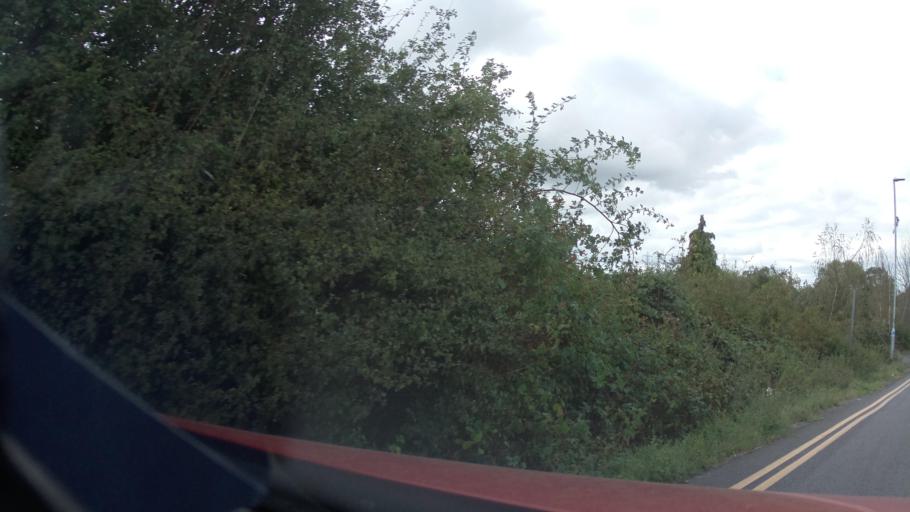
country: GB
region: England
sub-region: Leicestershire
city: Loughborough
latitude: 52.7832
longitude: -1.2014
